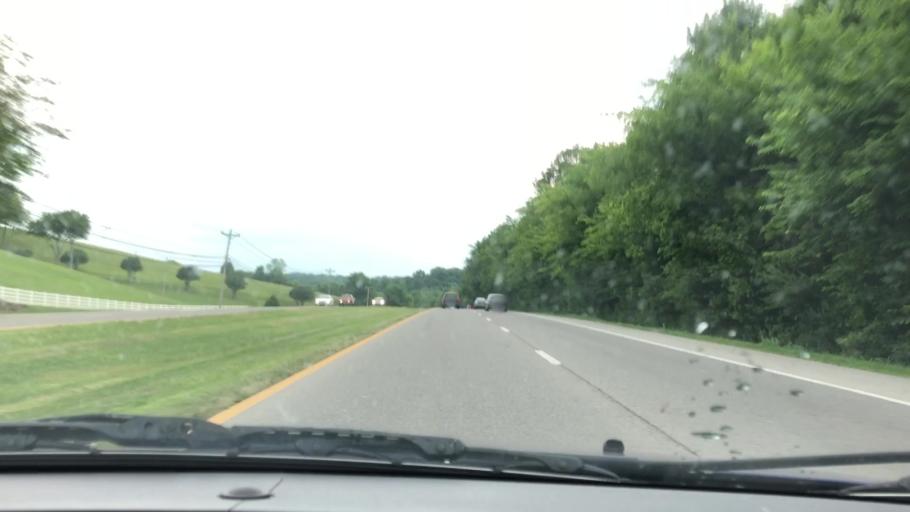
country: US
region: Tennessee
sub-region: Maury County
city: Columbia
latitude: 35.6583
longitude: -87.0080
